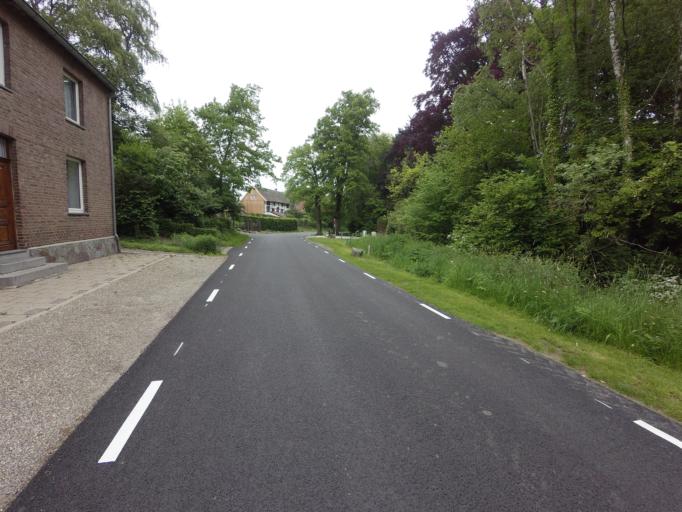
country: BE
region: Wallonia
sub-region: Province de Liege
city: Plombieres
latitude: 50.7599
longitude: 5.9113
